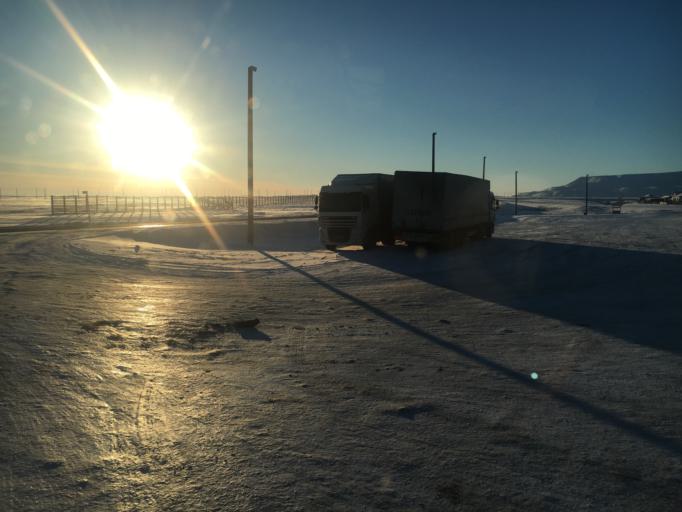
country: KZ
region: Aqtoebe
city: Khromtau
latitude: 50.2508
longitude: 58.4989
